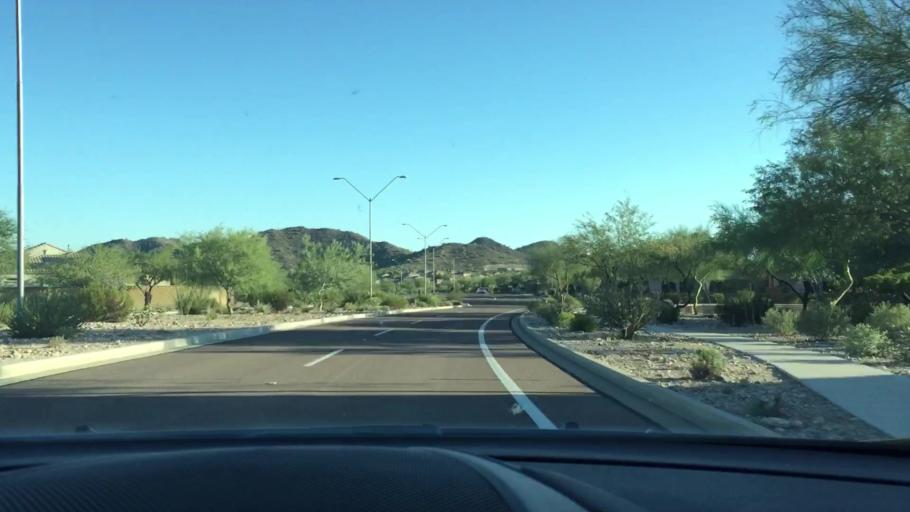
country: US
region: Arizona
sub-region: Maricopa County
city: Sun City West
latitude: 33.7343
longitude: -112.2539
